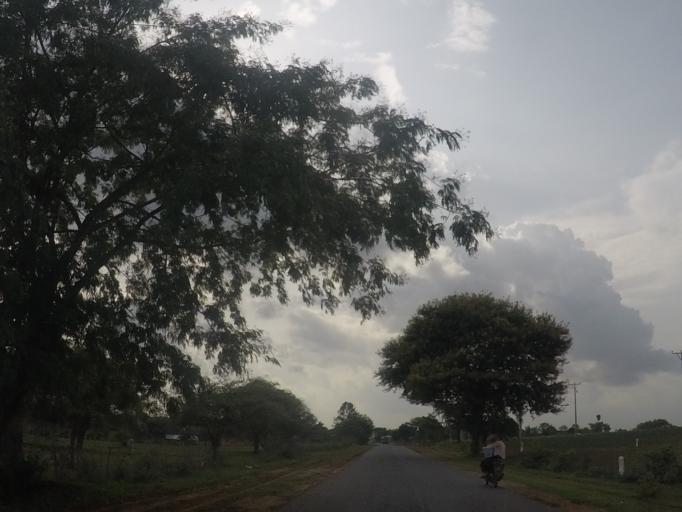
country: MM
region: Mandalay
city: Yamethin
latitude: 20.4996
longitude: 95.7917
